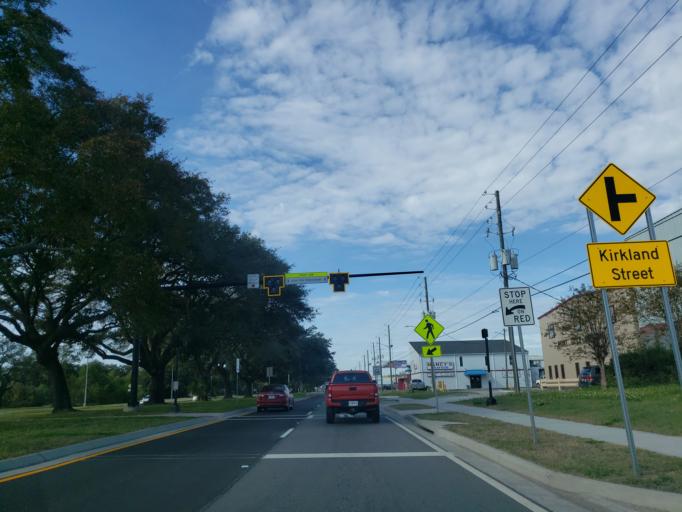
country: US
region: Georgia
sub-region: Chatham County
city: Savannah
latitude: 32.0871
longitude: -81.1139
